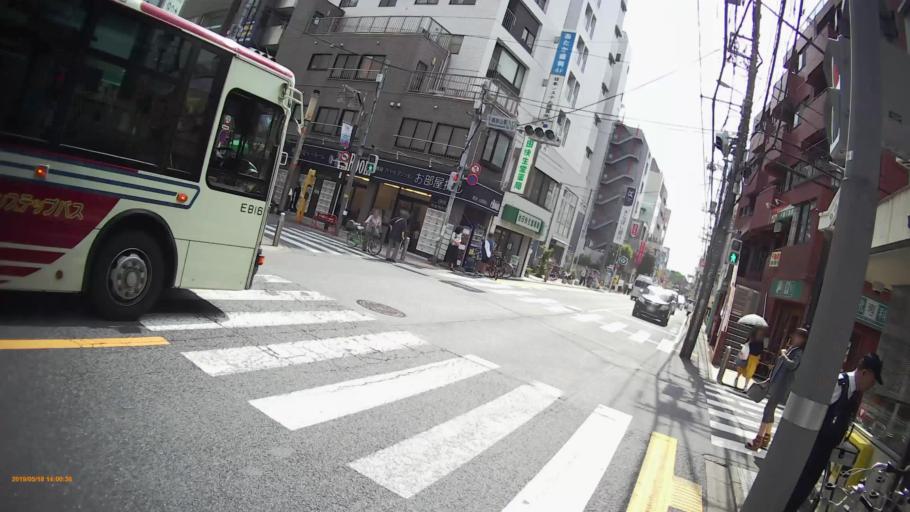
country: JP
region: Tokyo
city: Mitaka-shi
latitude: 35.6697
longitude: 139.6008
